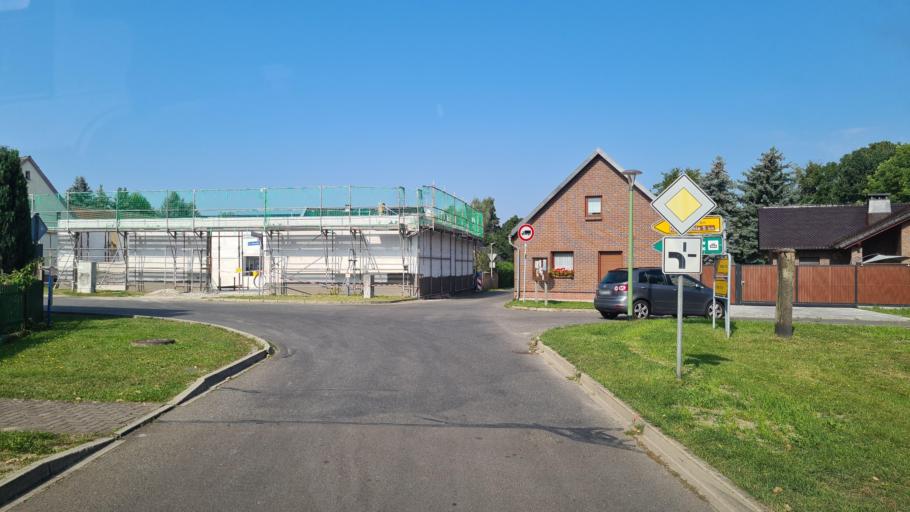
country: DE
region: Brandenburg
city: Kolkwitz
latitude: 51.7486
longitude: 14.2051
